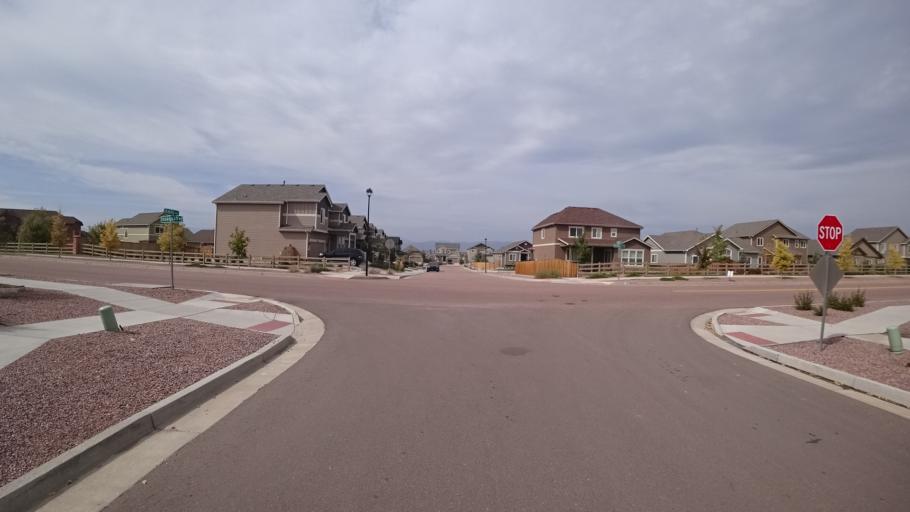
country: US
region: Colorado
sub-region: El Paso County
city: Cimarron Hills
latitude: 38.9252
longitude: -104.6853
